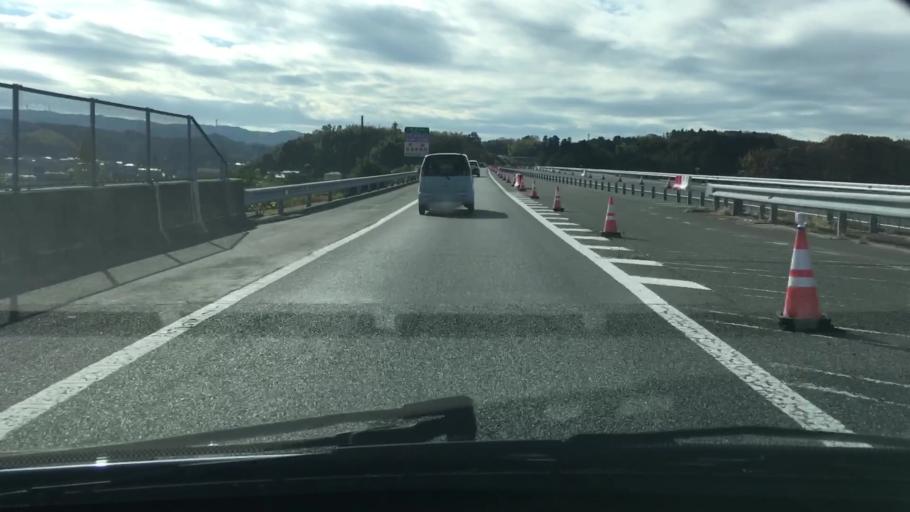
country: JP
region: Chiba
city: Kimitsu
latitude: 35.3080
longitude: 139.9423
